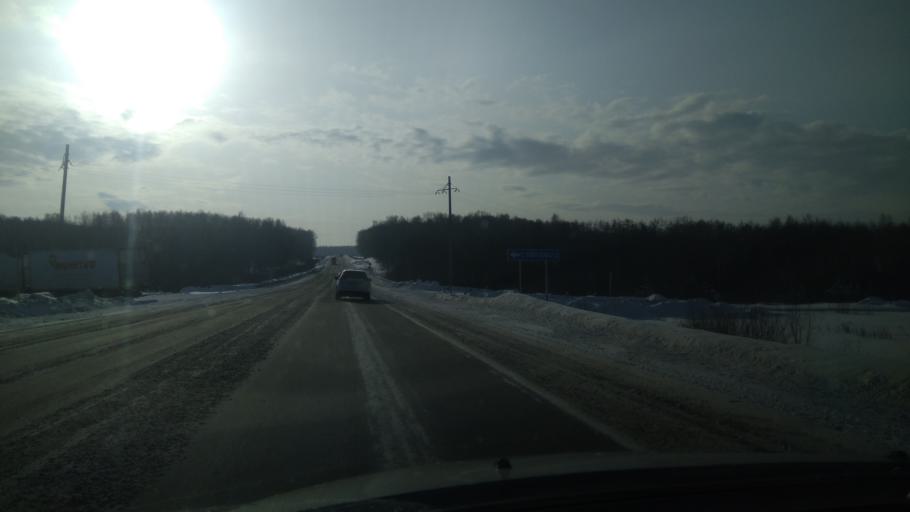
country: RU
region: Sverdlovsk
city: Bogdanovich
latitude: 56.7894
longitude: 62.0003
